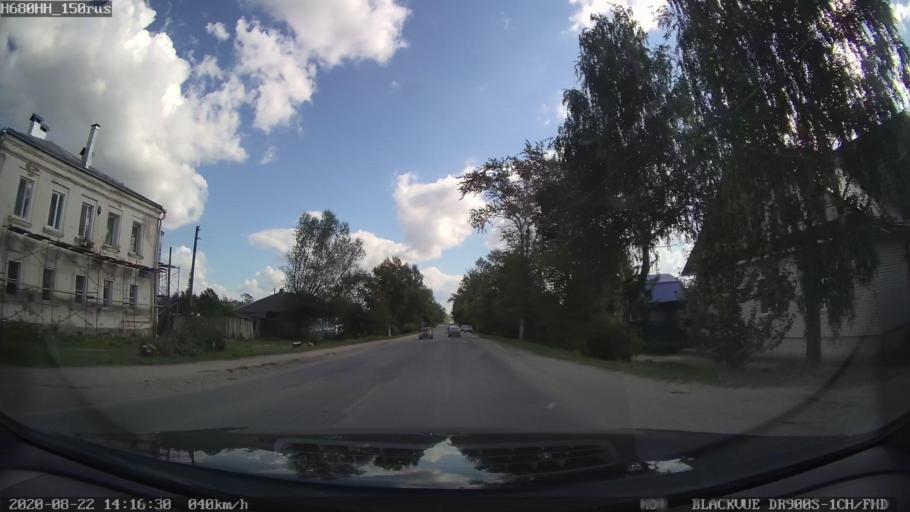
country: RU
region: Tverskaya
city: Bezhetsk
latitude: 57.7758
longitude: 36.6978
